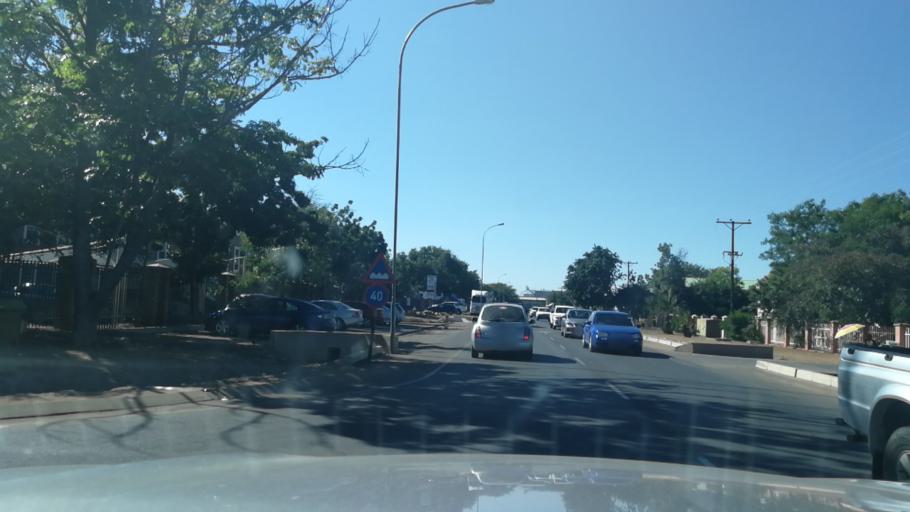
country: BW
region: South East
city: Gaborone
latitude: -24.6936
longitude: 25.8846
